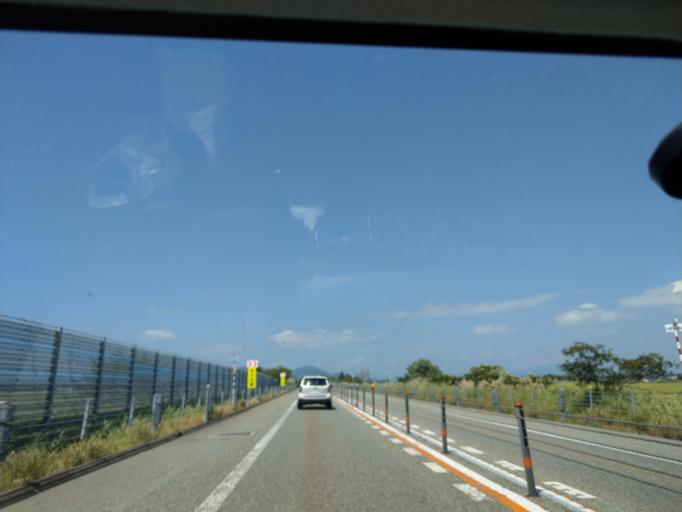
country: JP
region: Akita
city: Omagari
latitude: 39.3768
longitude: 140.4821
